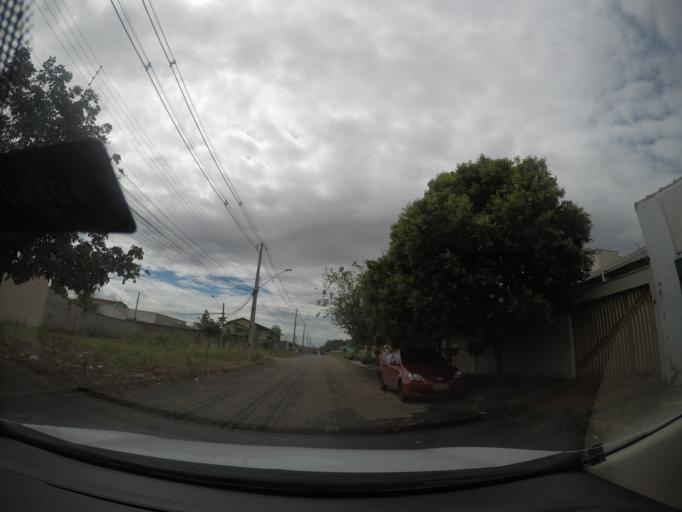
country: BR
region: Goias
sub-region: Goiania
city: Goiania
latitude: -16.7238
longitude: -49.3496
